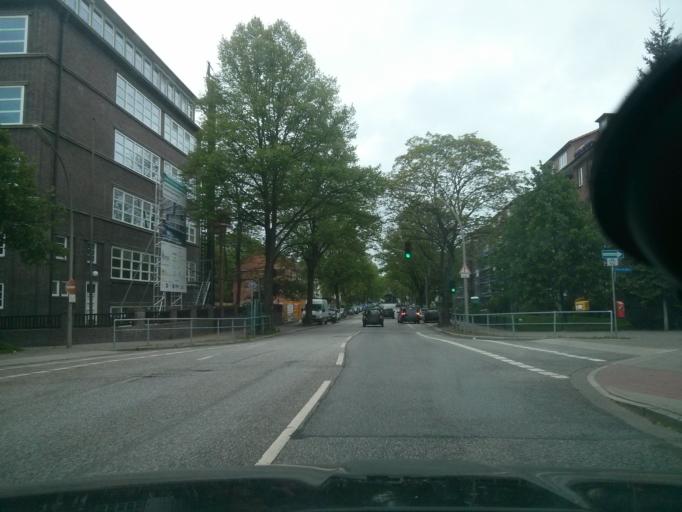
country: DE
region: Hamburg
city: Borgfelde
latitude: 53.5709
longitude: 10.0400
